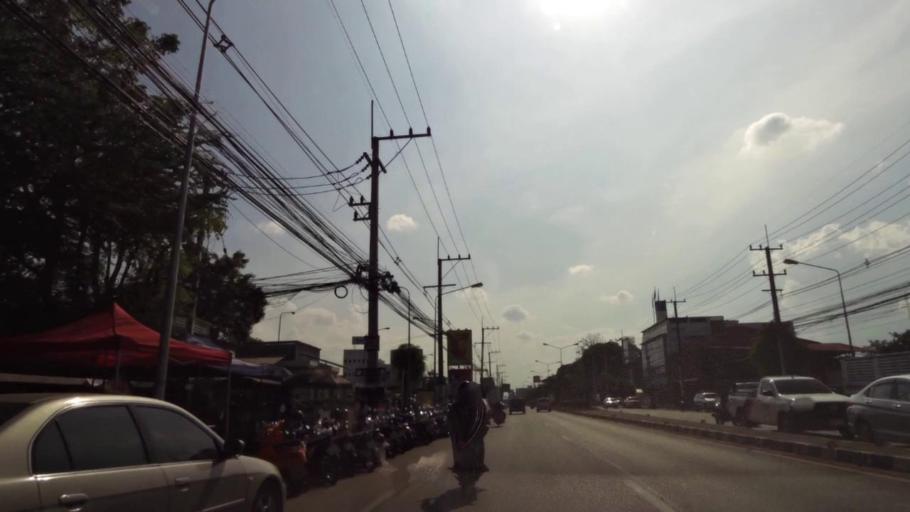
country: TH
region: Phrae
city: Phrae
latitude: 18.1291
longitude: 100.1439
